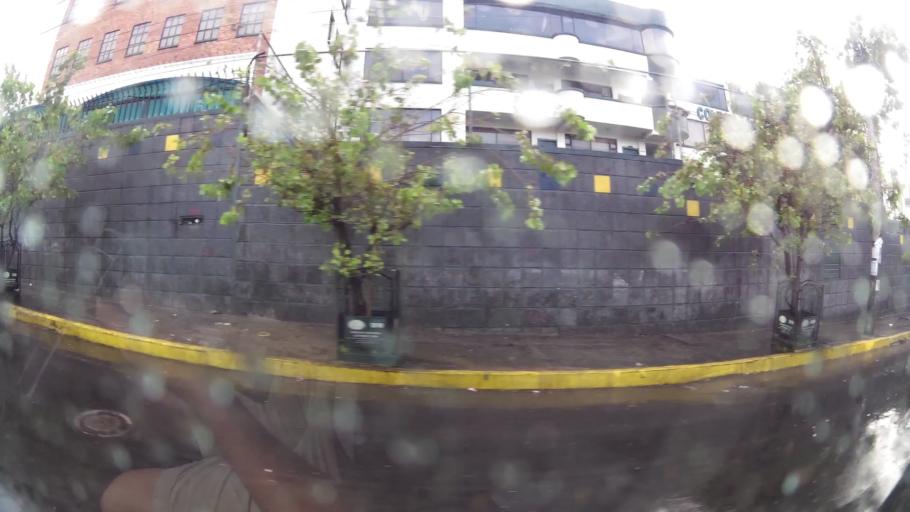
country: EC
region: Pichincha
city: Quito
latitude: -0.1043
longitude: -78.4978
